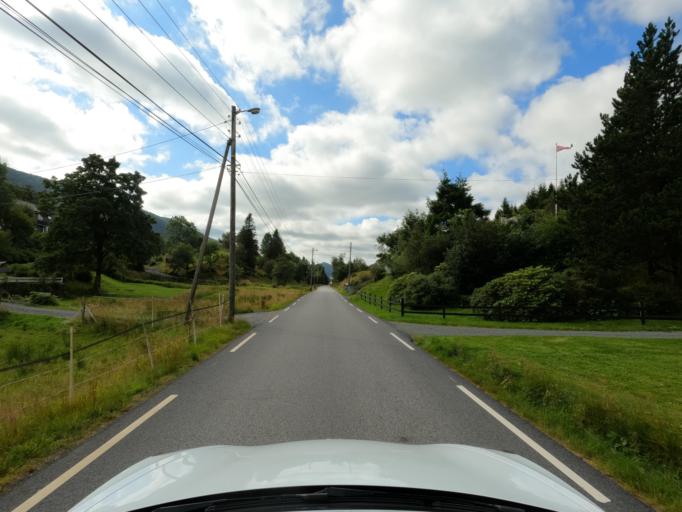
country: NO
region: Hordaland
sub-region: Os
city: Syfteland
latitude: 60.2891
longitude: 5.4751
